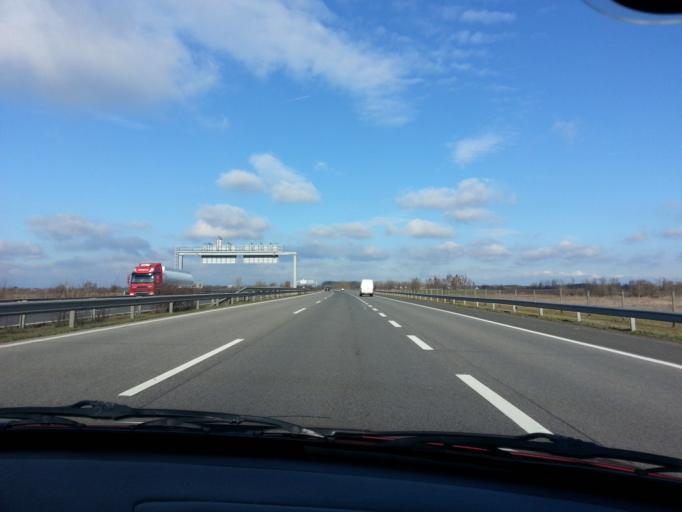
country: HU
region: Csongrad
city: Szatymaz
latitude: 46.3086
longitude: 20.0415
